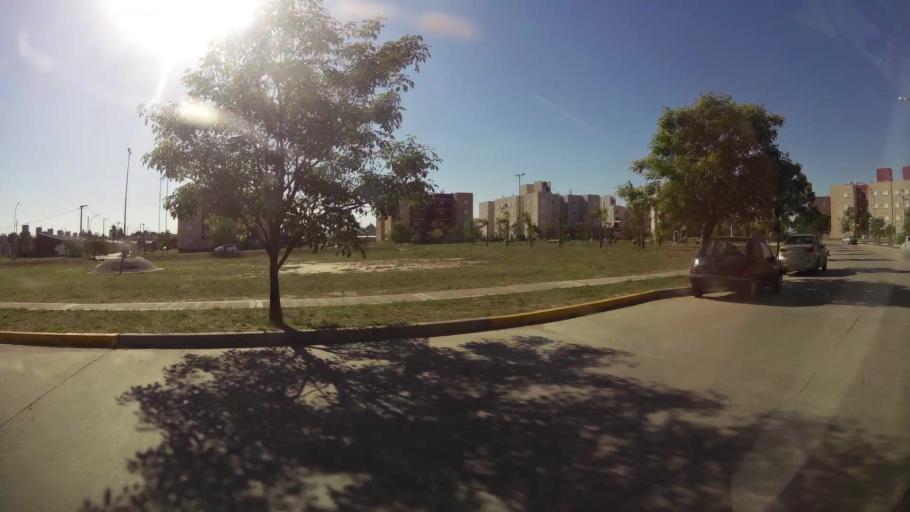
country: AR
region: Cordoba
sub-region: Departamento de Capital
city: Cordoba
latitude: -31.3566
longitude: -64.1912
